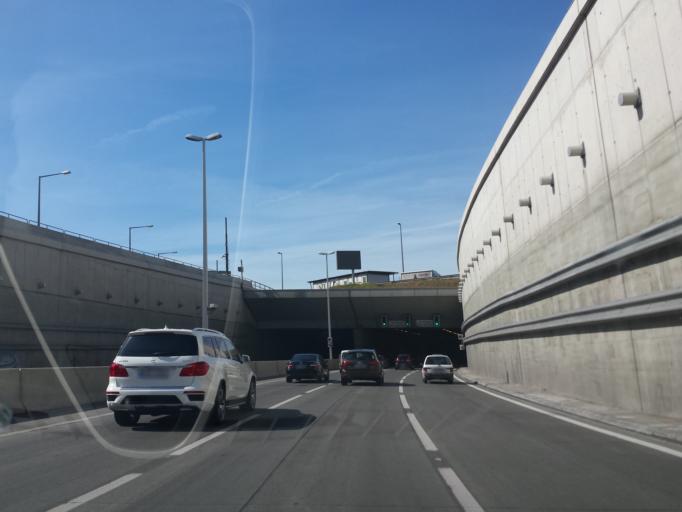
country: AT
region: Lower Austria
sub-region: Politischer Bezirk Wien-Umgebung
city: Leopoldsdorf
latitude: 48.1624
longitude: 16.3851
